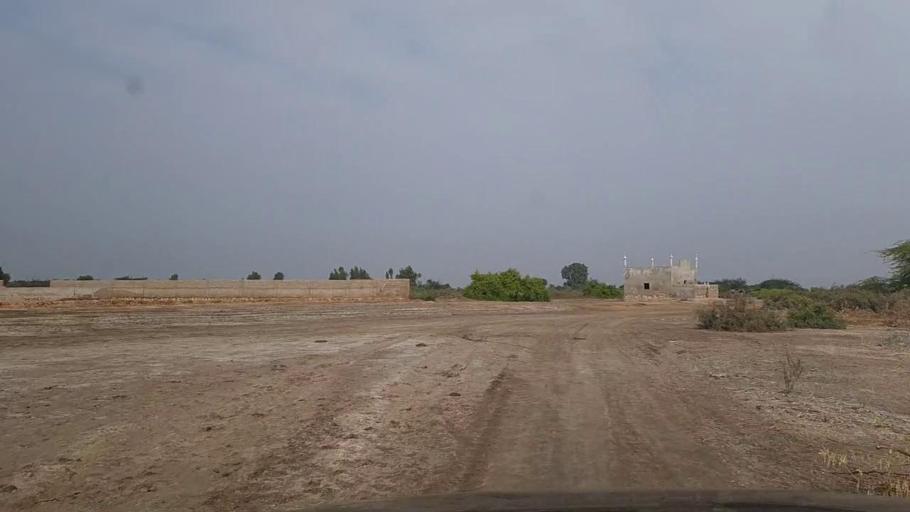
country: PK
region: Sindh
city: Thatta
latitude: 24.7526
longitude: 67.8272
